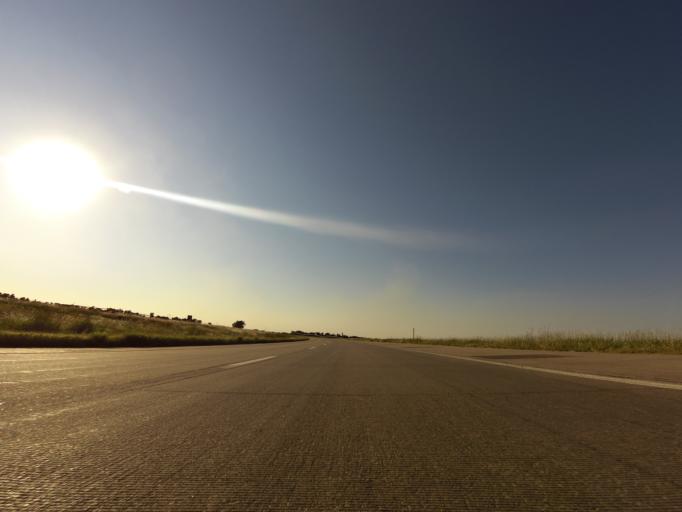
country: US
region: Kansas
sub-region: Sedgwick County
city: Colwich
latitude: 37.8725
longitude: -97.6268
